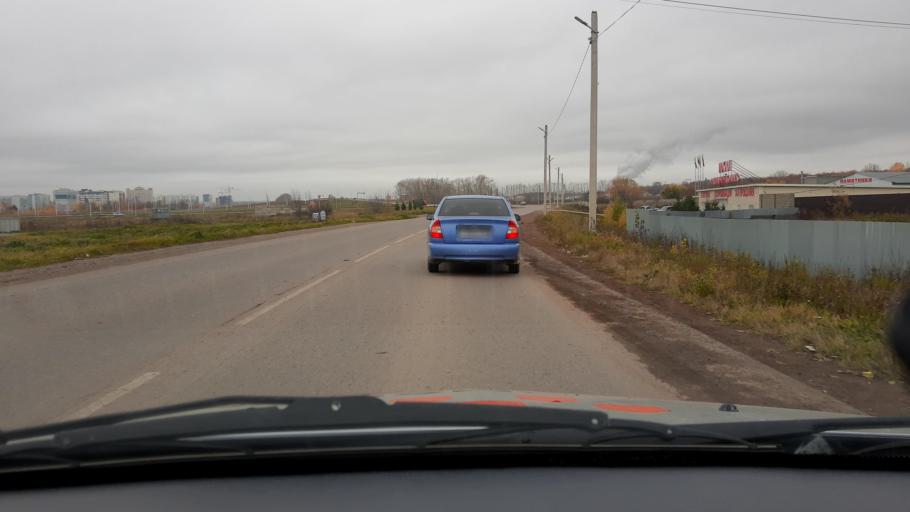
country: RU
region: Bashkortostan
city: Mikhaylovka
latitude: 54.8006
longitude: 55.8769
